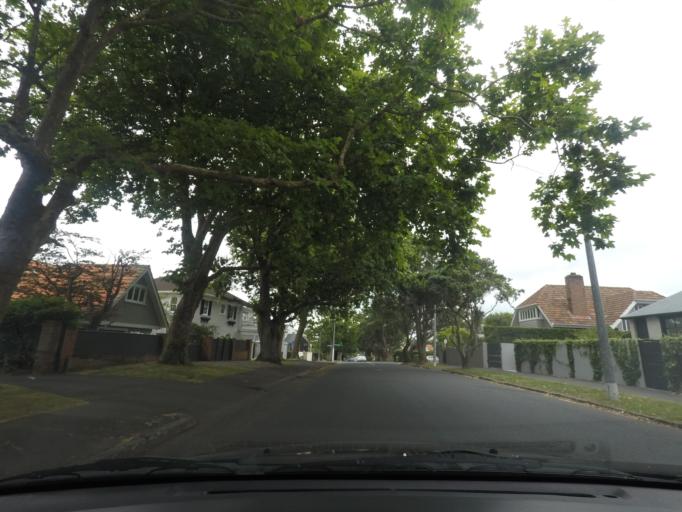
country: NZ
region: Auckland
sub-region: Auckland
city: Auckland
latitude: -36.8530
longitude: 174.7897
